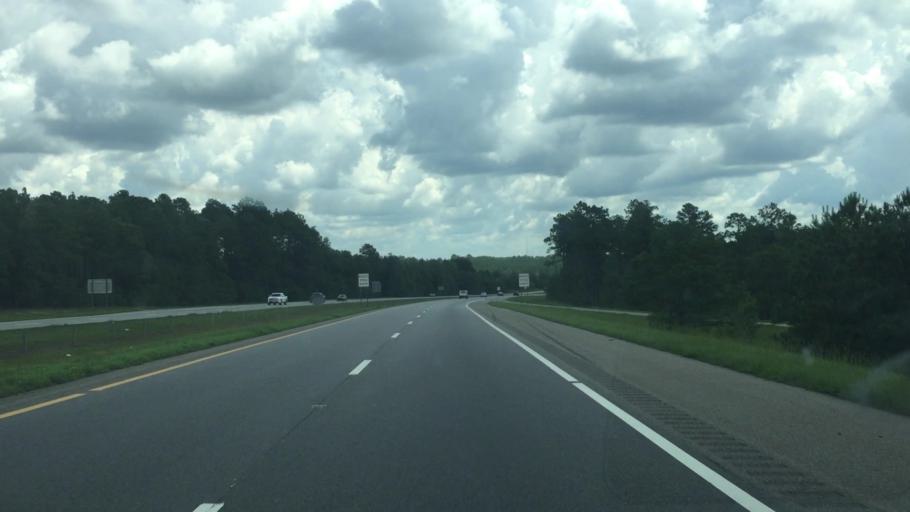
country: US
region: North Carolina
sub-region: Richmond County
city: Hamlet
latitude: 34.8649
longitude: -79.6685
